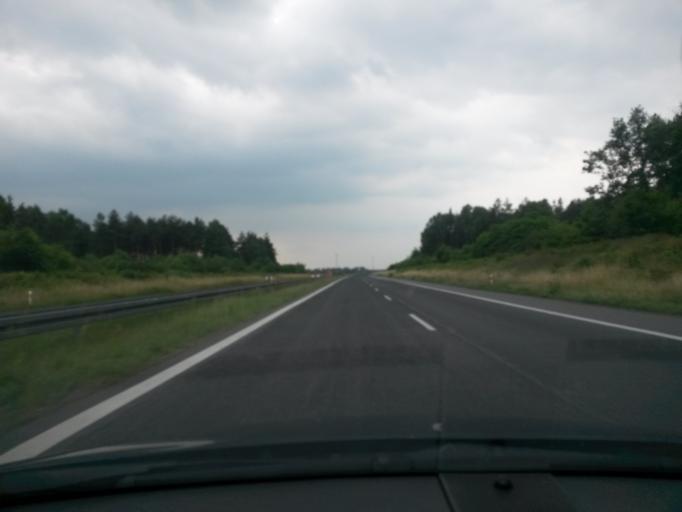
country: PL
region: Silesian Voivodeship
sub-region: Powiat czestochowski
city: Borowno
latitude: 50.9831
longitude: 19.2794
